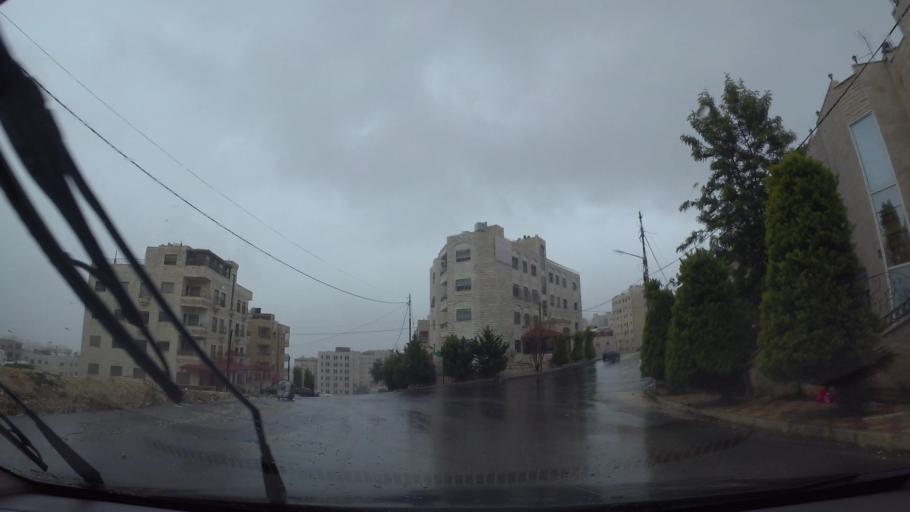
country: JO
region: Amman
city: Al Jubayhah
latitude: 32.0245
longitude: 35.8863
